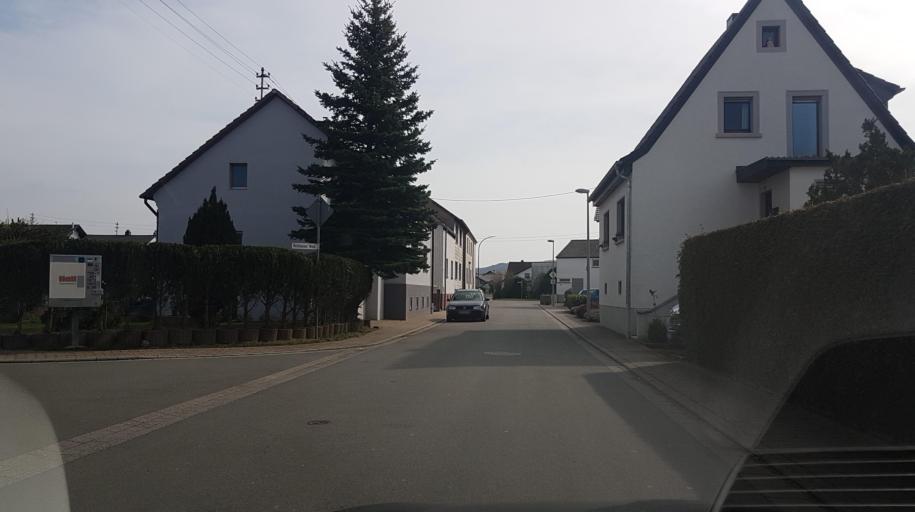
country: DE
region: Rheinland-Pfalz
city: Bruchmuhlbach-Miesau
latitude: 49.4055
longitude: 7.4427
